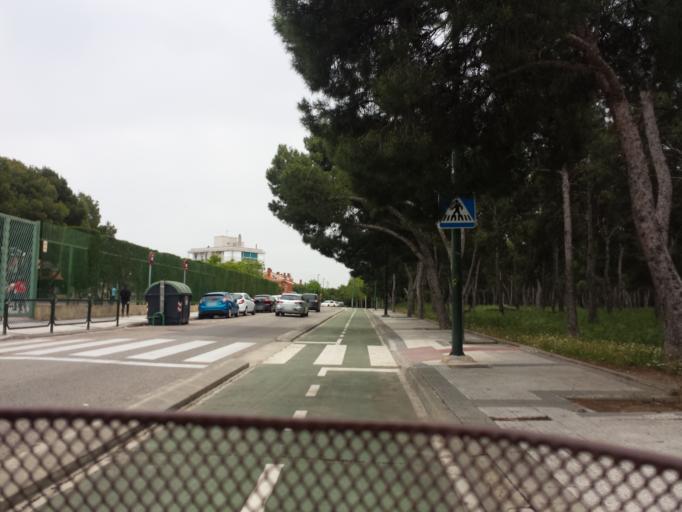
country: ES
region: Aragon
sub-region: Provincia de Zaragoza
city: Zaragoza
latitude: 41.6256
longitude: -0.8825
